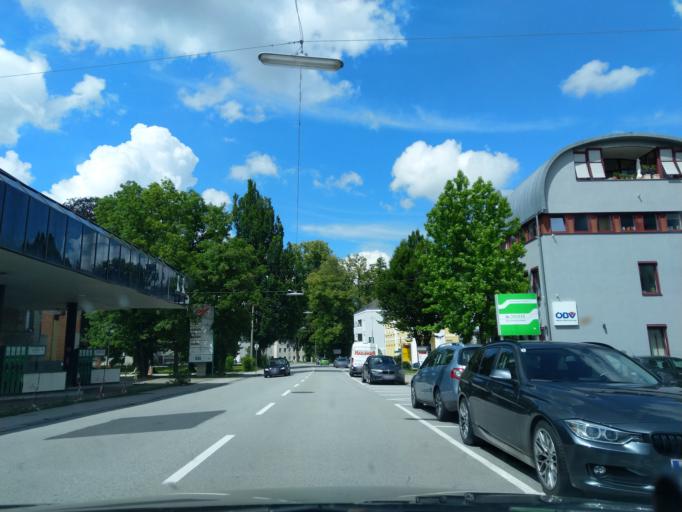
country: AT
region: Upper Austria
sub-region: Politischer Bezirk Ried im Innkreis
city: Ried im Innkreis
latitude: 48.2038
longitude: 13.4890
